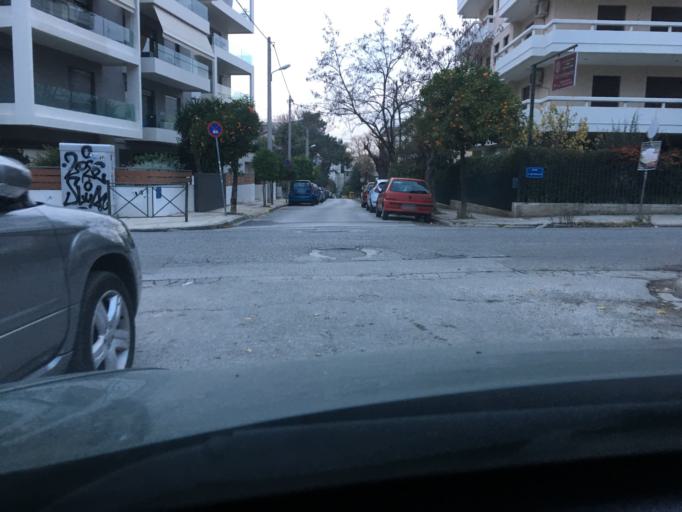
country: GR
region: Attica
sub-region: Nomarchia Athinas
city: Khalandrion
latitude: 38.0271
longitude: 23.8004
